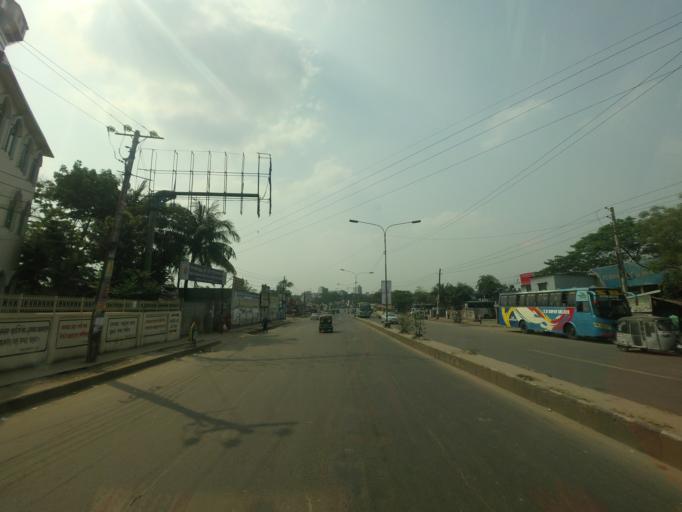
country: BD
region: Dhaka
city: Azimpur
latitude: 23.7818
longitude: 90.3514
